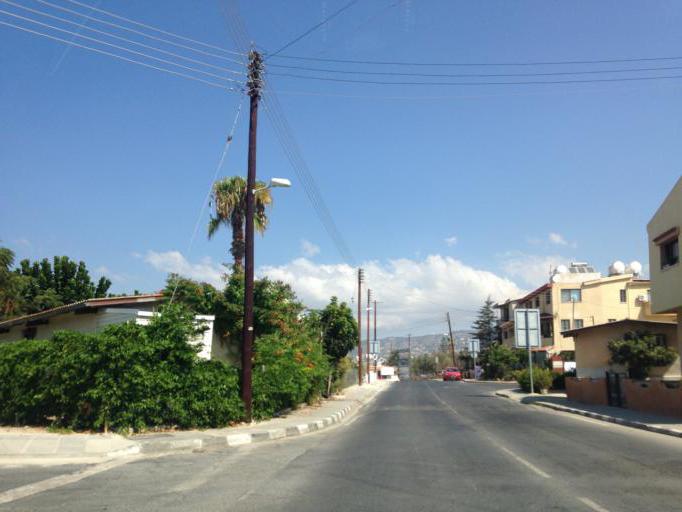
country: CY
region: Pafos
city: Chlorakas
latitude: 34.8013
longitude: 32.4068
